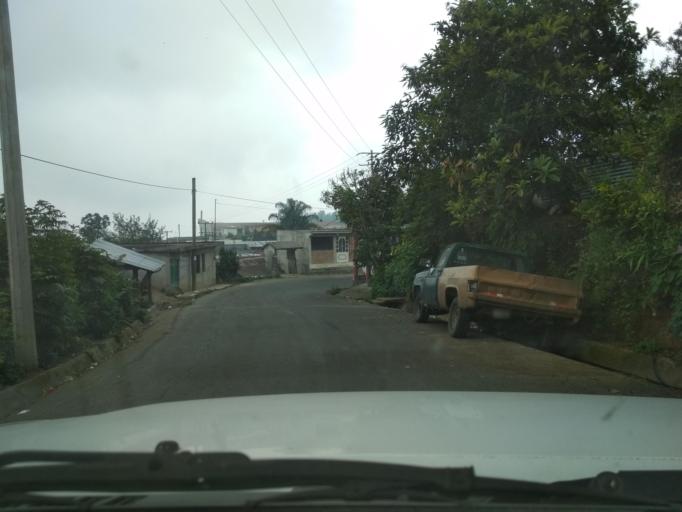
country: MX
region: Veracruz
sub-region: La Perla
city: Metlac Hernandez (Metlac Primero)
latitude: 18.9605
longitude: -97.1584
